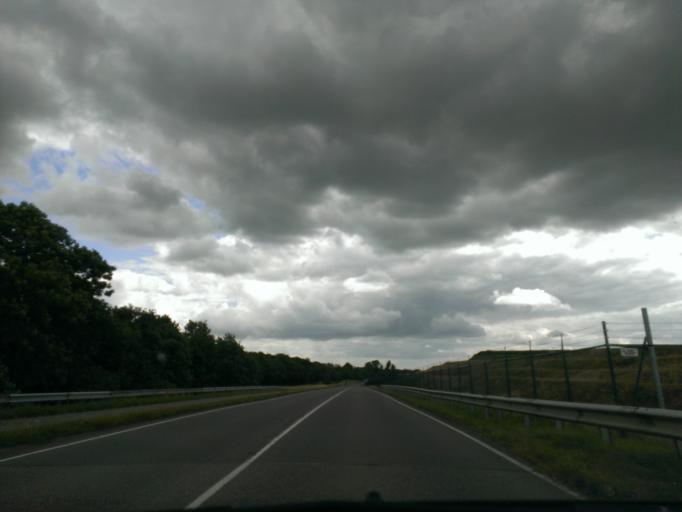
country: NL
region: Gelderland
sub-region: Gemeente Voorst
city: Twello
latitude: 52.2063
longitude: 6.0852
